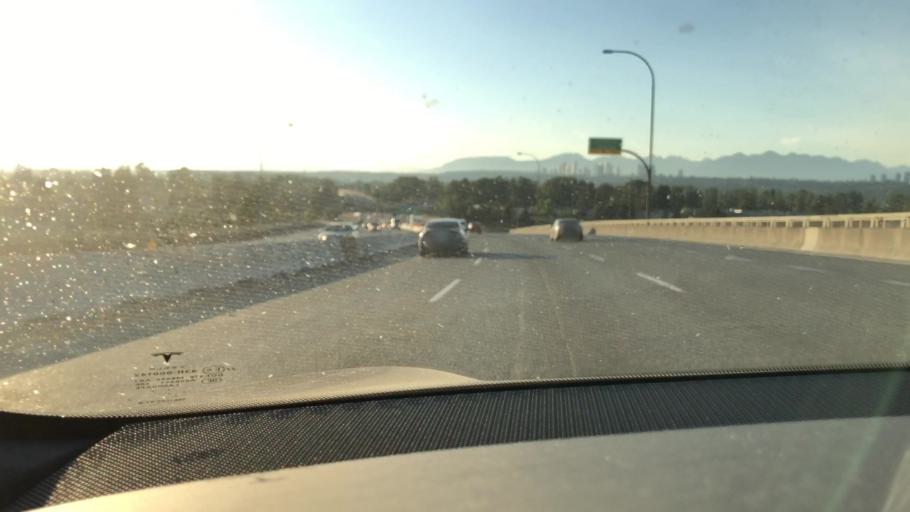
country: CA
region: British Columbia
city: Delta
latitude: 49.1680
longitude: -122.9464
